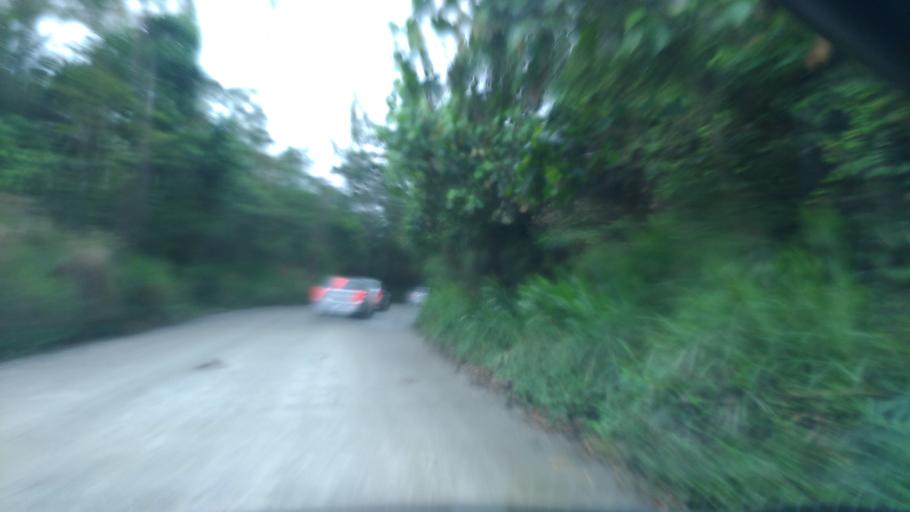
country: BR
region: Sao Paulo
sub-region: Sao Bernardo Do Campo
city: Sao Bernardo do Campo
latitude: -23.7422
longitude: -46.5126
